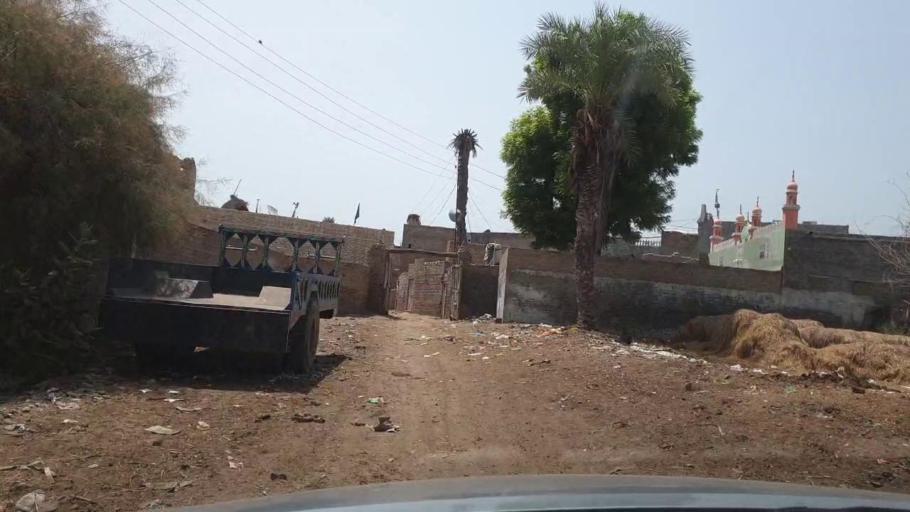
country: PK
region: Sindh
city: Madeji
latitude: 27.7866
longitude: 68.4338
